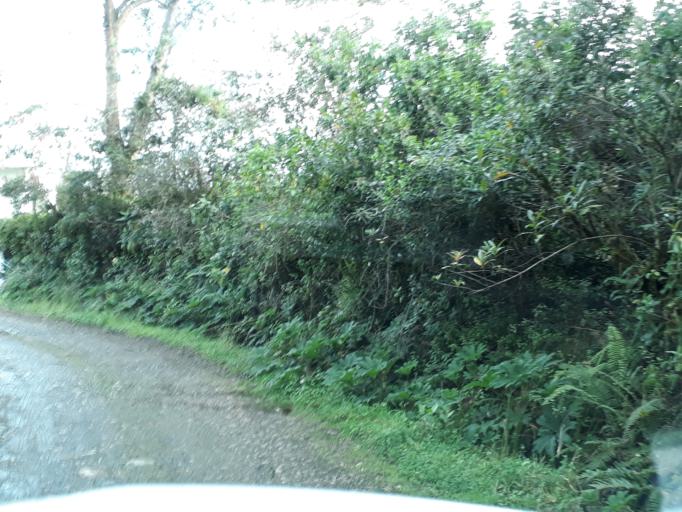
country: CO
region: Cundinamarca
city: Guasca
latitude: 4.8338
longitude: -73.7734
